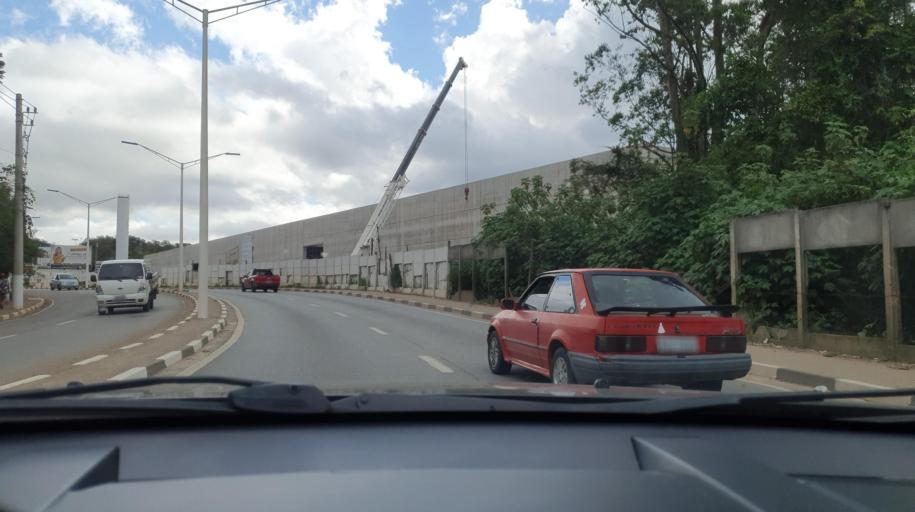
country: BR
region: Sao Paulo
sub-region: Vargem Grande Paulista
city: Vargem Grande Paulista
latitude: -23.6424
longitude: -46.9907
